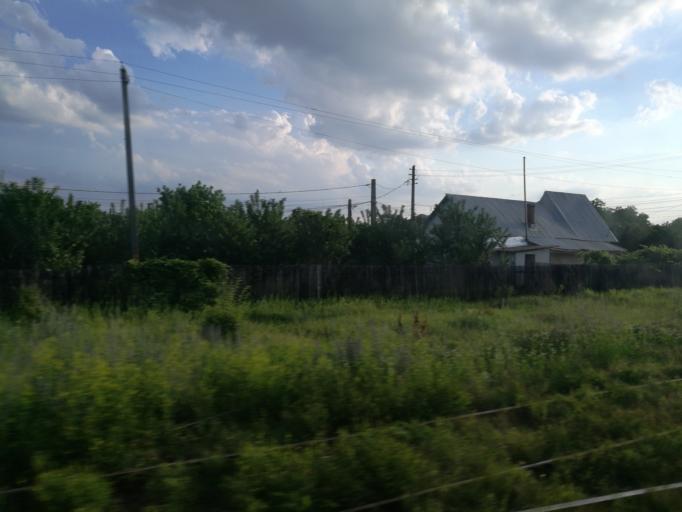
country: RO
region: Arges
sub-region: Comuna Leordeni
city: Leordeni
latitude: 44.7845
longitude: 25.1211
